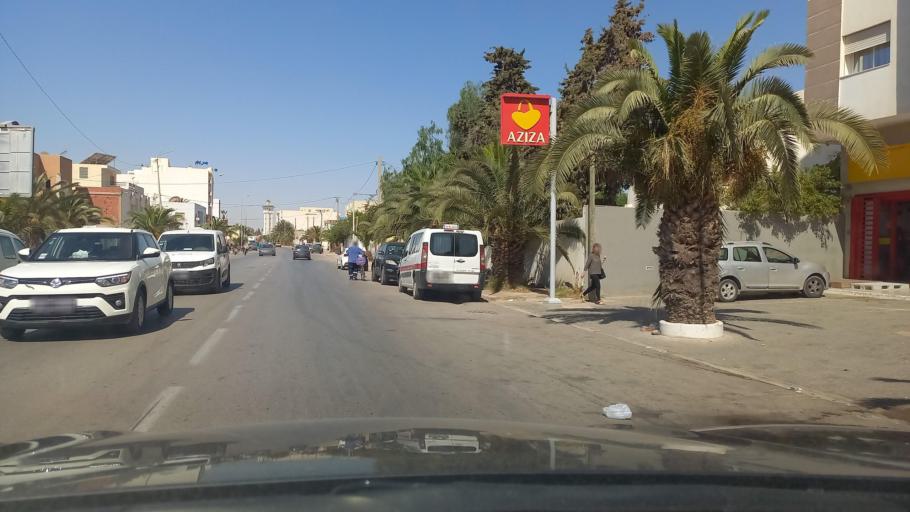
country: TN
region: Safaqis
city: Sfax
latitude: 34.7308
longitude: 10.7358
